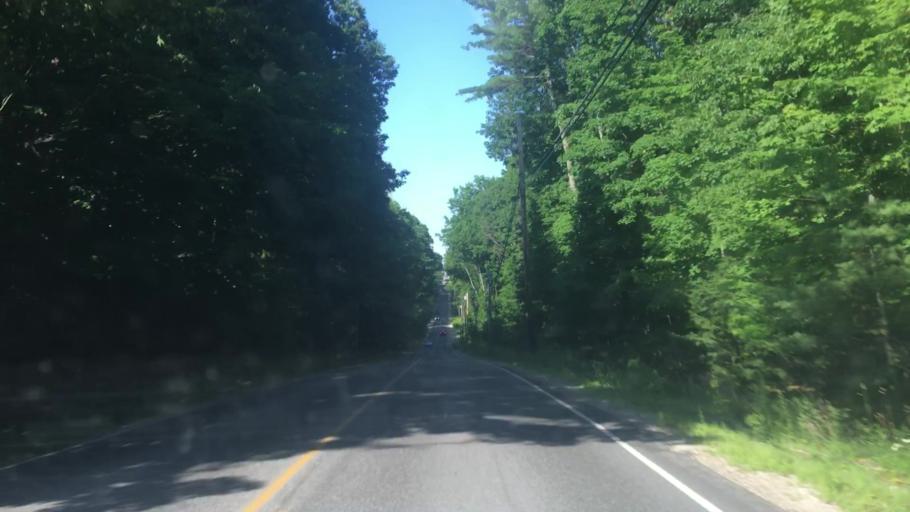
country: US
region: Maine
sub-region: York County
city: Buxton
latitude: 43.7260
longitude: -70.5607
